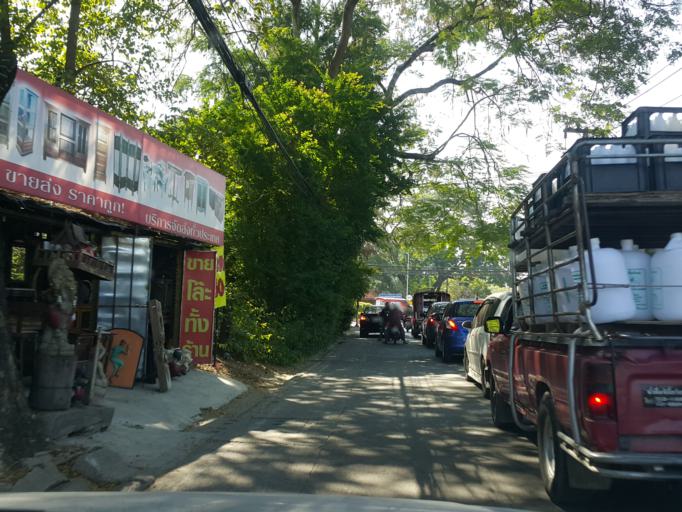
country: TH
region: Chiang Mai
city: Chiang Mai
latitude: 18.7858
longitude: 99.0178
